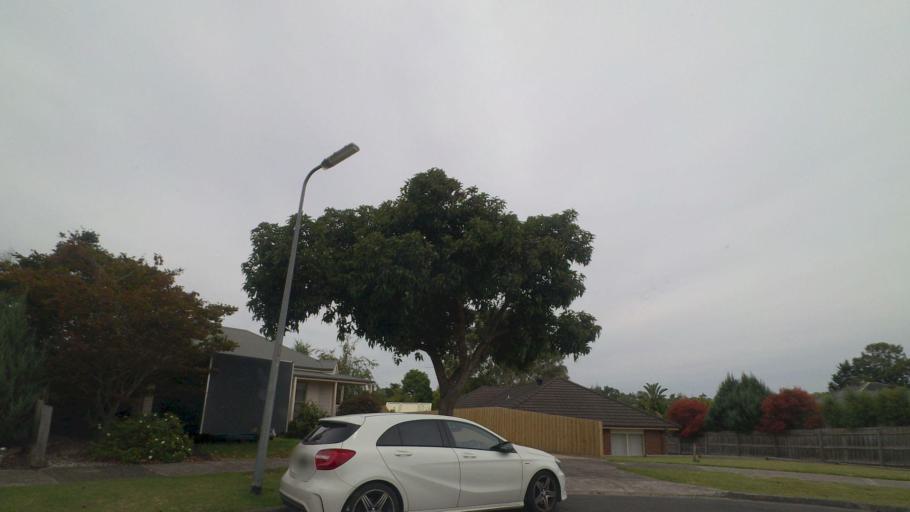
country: AU
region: Victoria
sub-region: Yarra Ranges
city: Kilsyth
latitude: -37.7831
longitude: 145.3353
